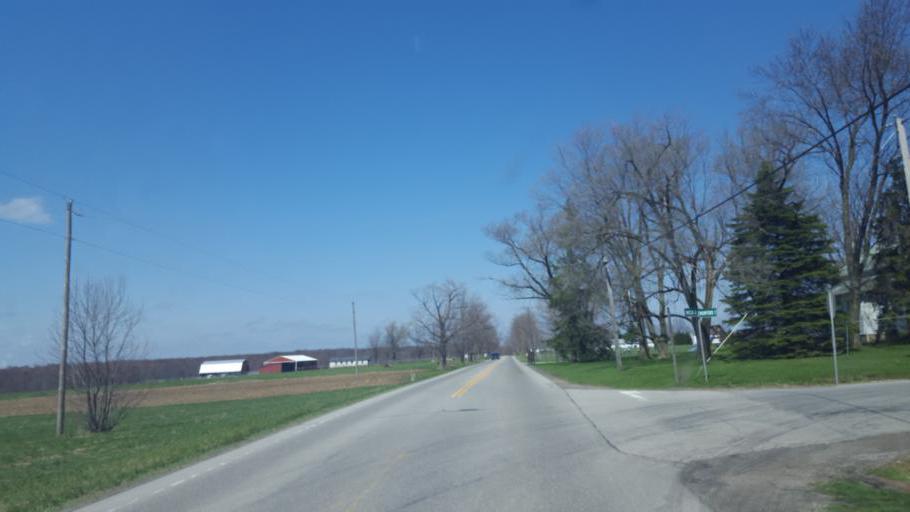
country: US
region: Ohio
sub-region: Geauga County
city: Middlefield
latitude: 41.4096
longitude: -81.1085
